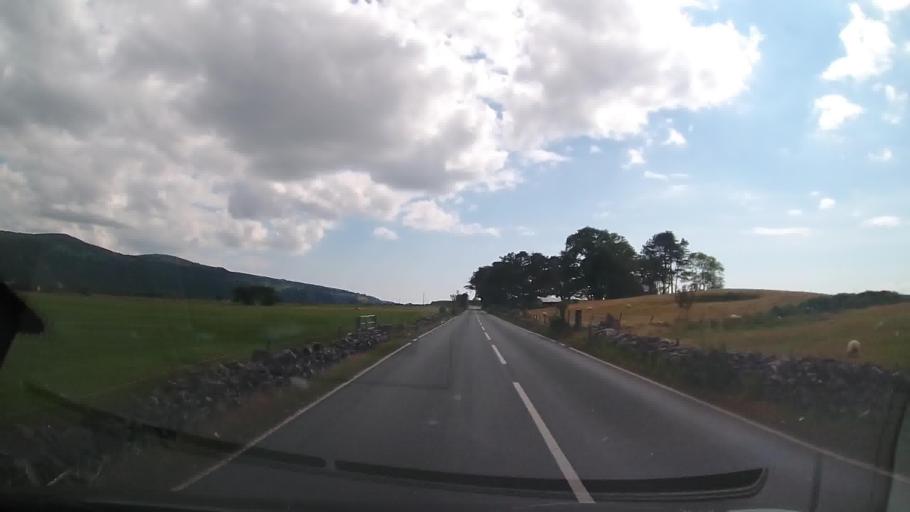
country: GB
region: Wales
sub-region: Gwynedd
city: Llanfair
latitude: 52.8881
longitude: -4.0971
